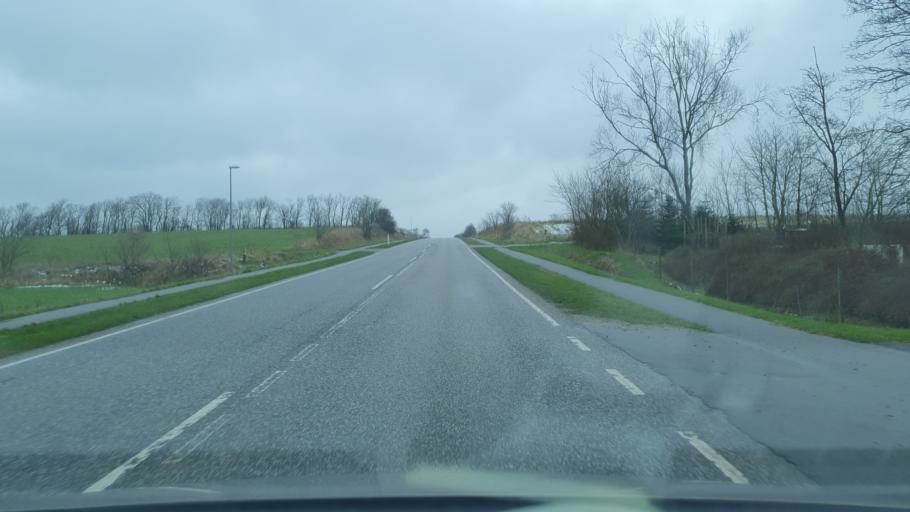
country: DK
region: North Denmark
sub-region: Jammerbugt Kommune
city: Fjerritslev
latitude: 57.0988
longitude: 9.1493
